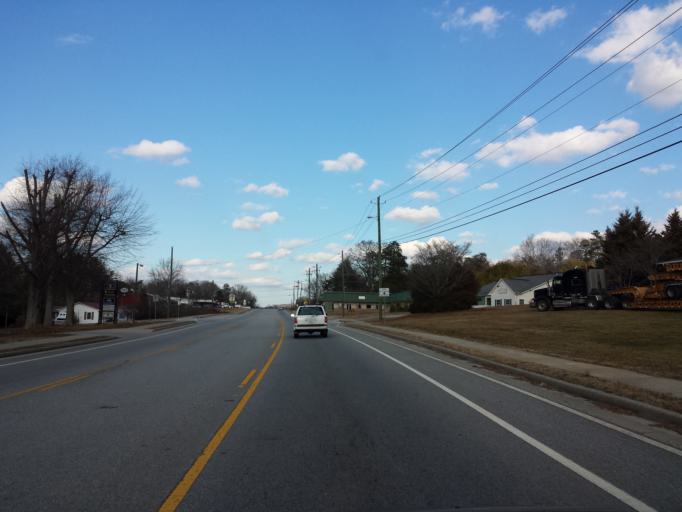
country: US
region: Georgia
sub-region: White County
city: Cleveland
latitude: 34.6070
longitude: -83.7591
